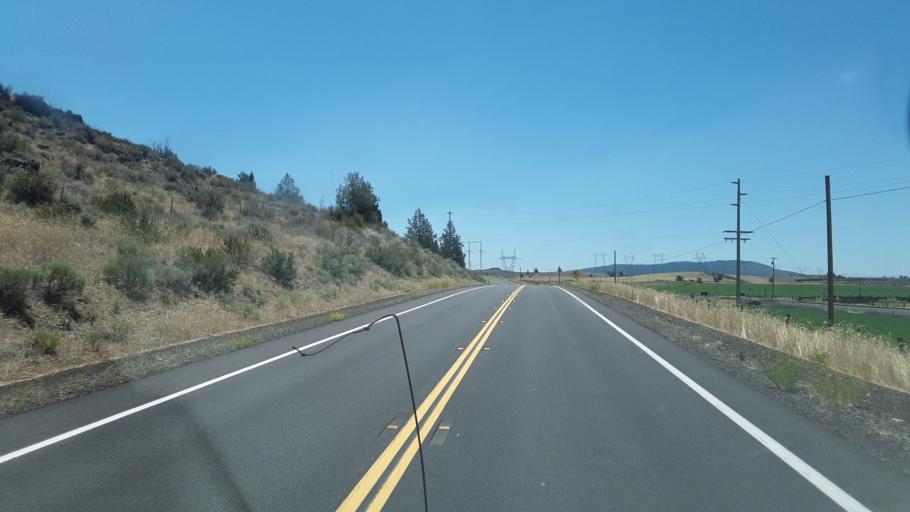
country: US
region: California
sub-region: Siskiyou County
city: Tulelake
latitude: 41.7241
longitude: -121.2952
